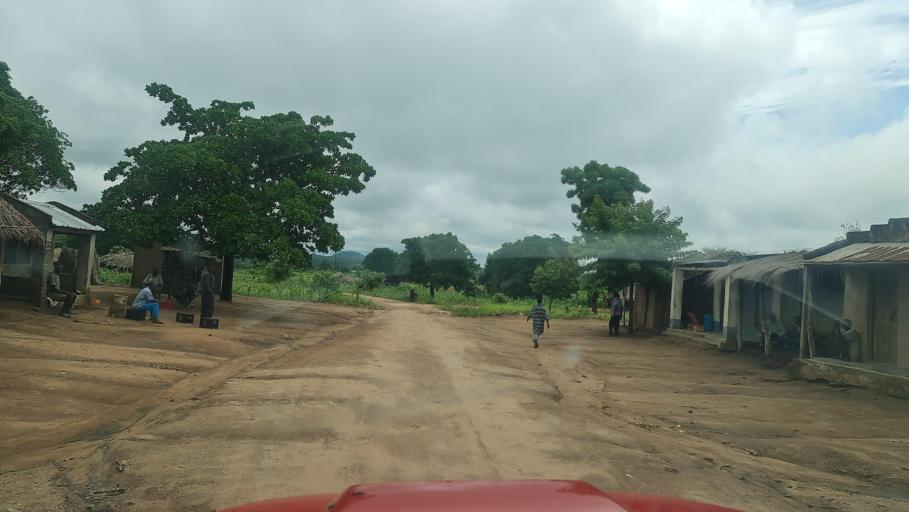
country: MW
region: Southern Region
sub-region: Nsanje District
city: Nsanje
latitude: -17.1859
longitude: 35.9222
